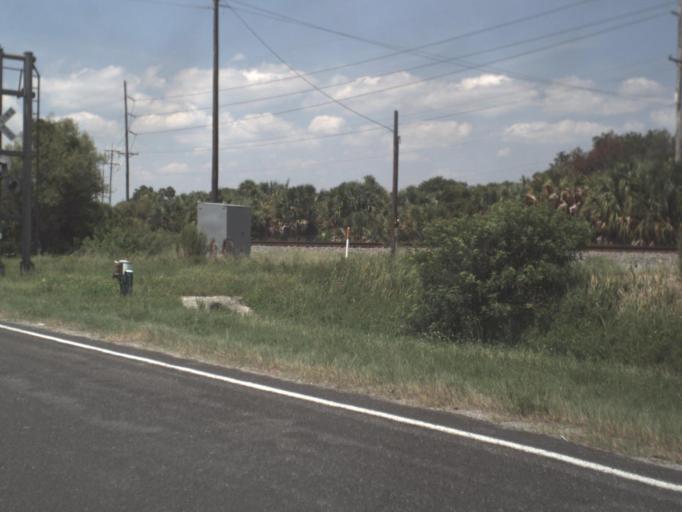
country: US
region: Florida
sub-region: Hillsborough County
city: Gibsonton
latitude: 27.8657
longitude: -82.3856
